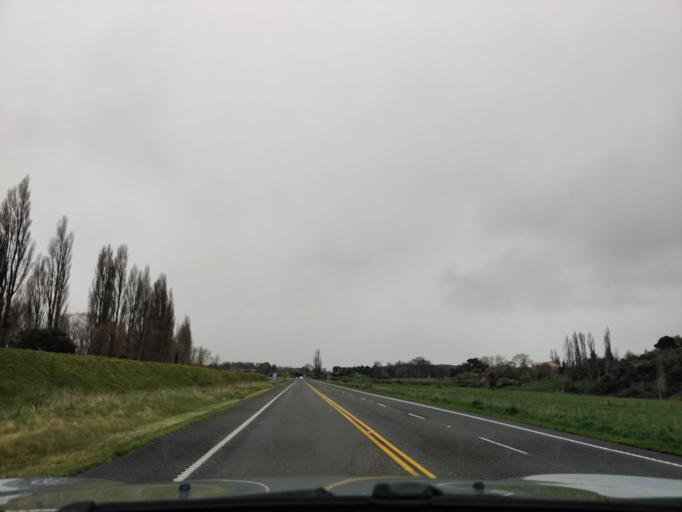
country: NZ
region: Hawke's Bay
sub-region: Hastings District
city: Hastings
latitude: -39.9844
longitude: 176.5088
